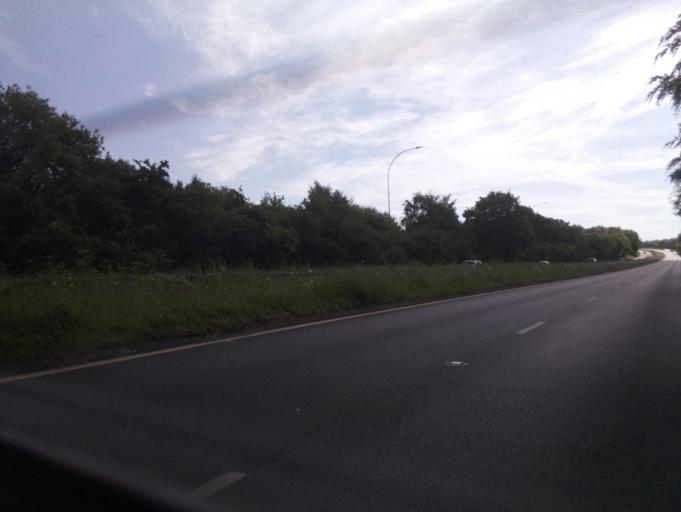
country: GB
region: England
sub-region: North Lincolnshire
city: Manton
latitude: 53.5608
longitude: -0.5978
